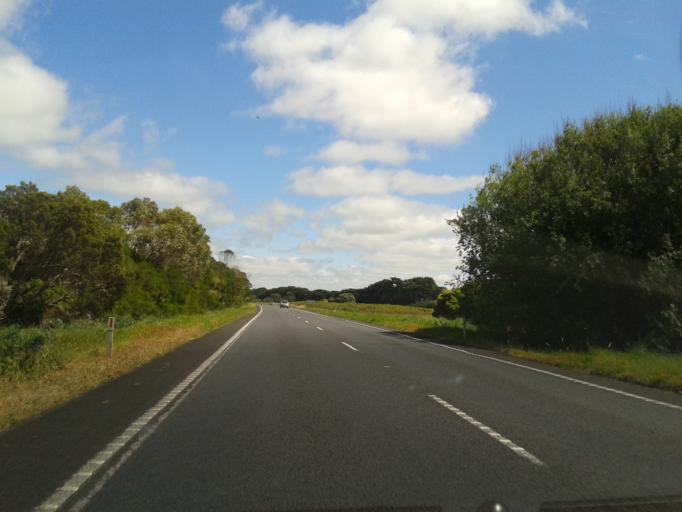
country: AU
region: Victoria
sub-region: Moyne
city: Port Fairy
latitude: -38.2679
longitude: 141.9570
